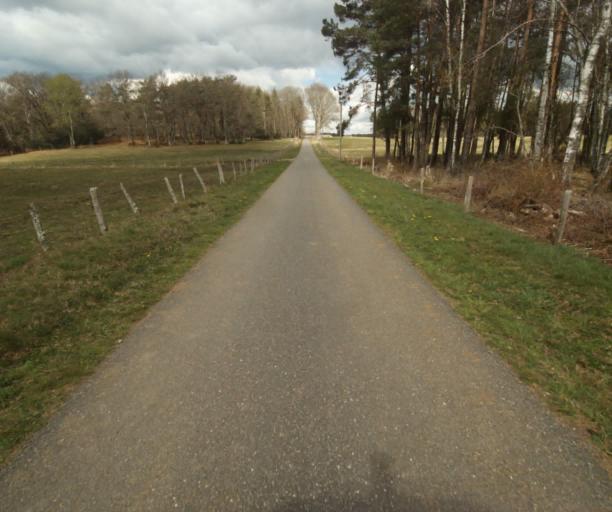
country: FR
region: Limousin
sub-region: Departement de la Correze
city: Correze
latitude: 45.2528
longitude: 1.9082
